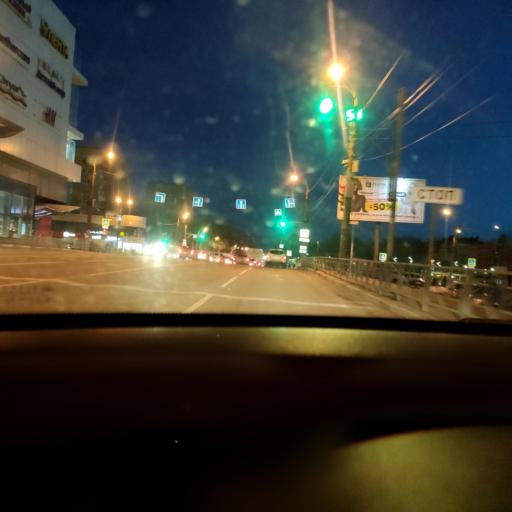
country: RU
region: Samara
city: Samara
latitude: 53.1907
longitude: 50.1911
